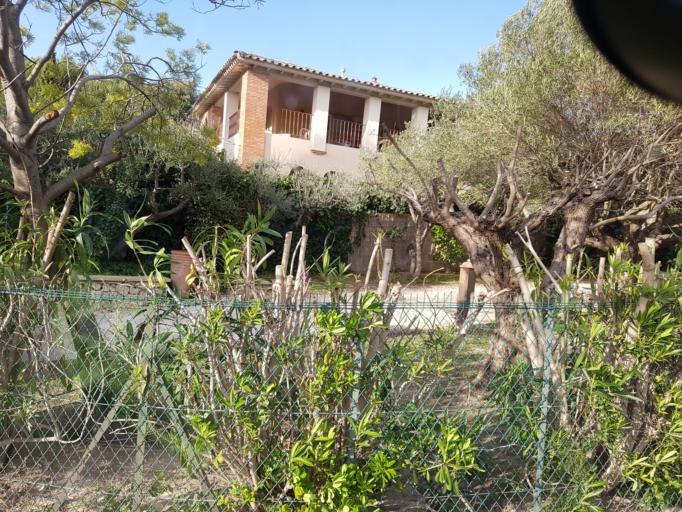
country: FR
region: Provence-Alpes-Cote d'Azur
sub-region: Departement des Bouches-du-Rhone
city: Cassis
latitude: 43.2110
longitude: 5.5472
